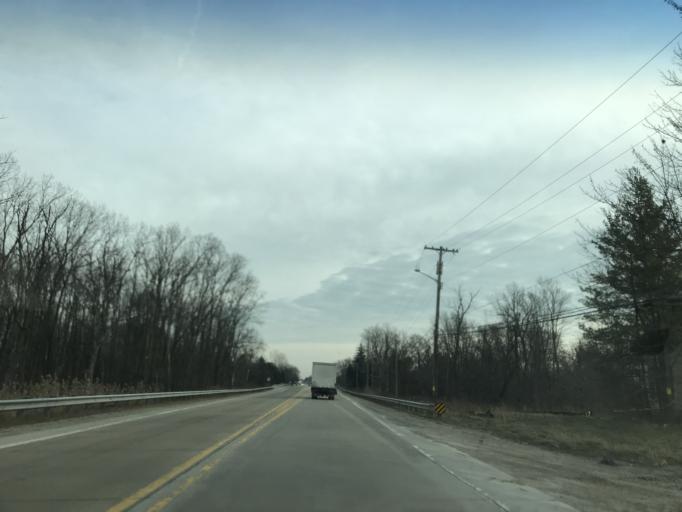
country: US
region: Michigan
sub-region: Macomb County
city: Mount Clemens
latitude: 42.6734
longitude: -82.8850
